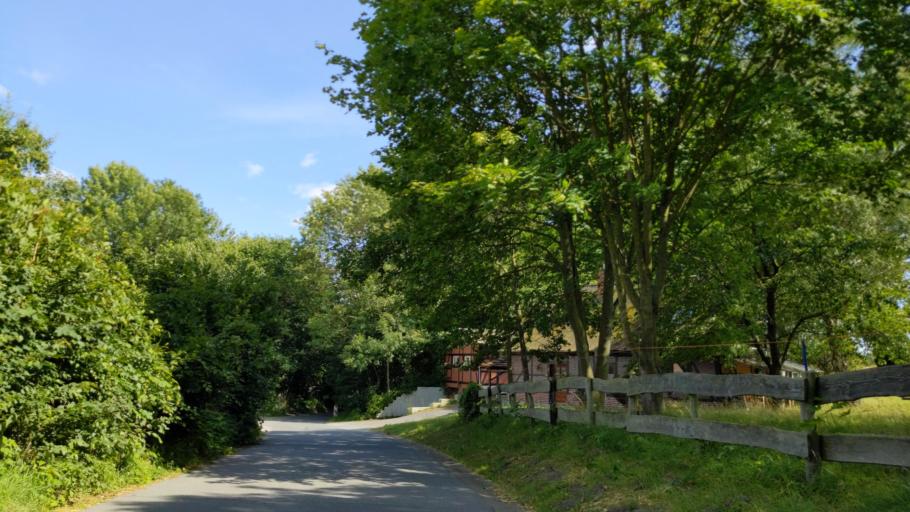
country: DE
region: Schleswig-Holstein
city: Altenkrempe
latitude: 54.1566
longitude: 10.8292
